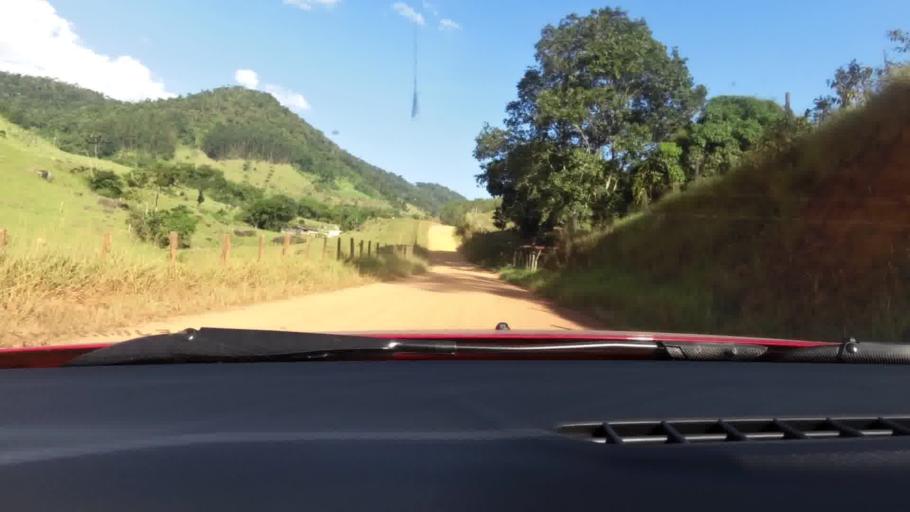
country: BR
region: Espirito Santo
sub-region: Guarapari
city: Guarapari
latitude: -20.5308
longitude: -40.5637
